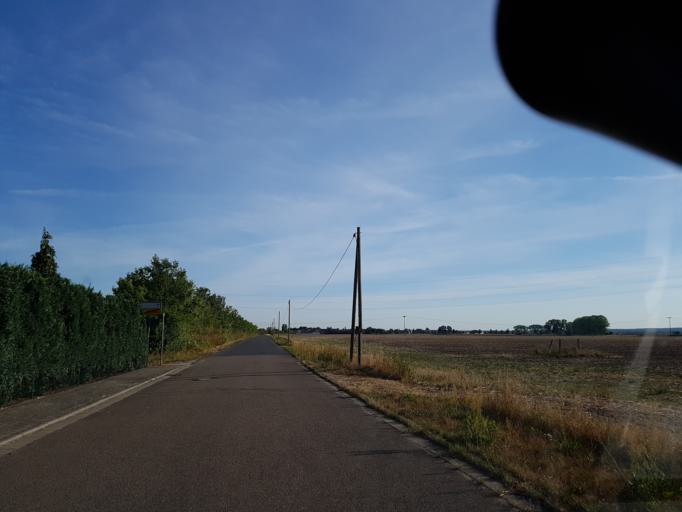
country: DE
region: Saxony
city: Nauwalde
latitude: 51.4487
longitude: 13.4197
